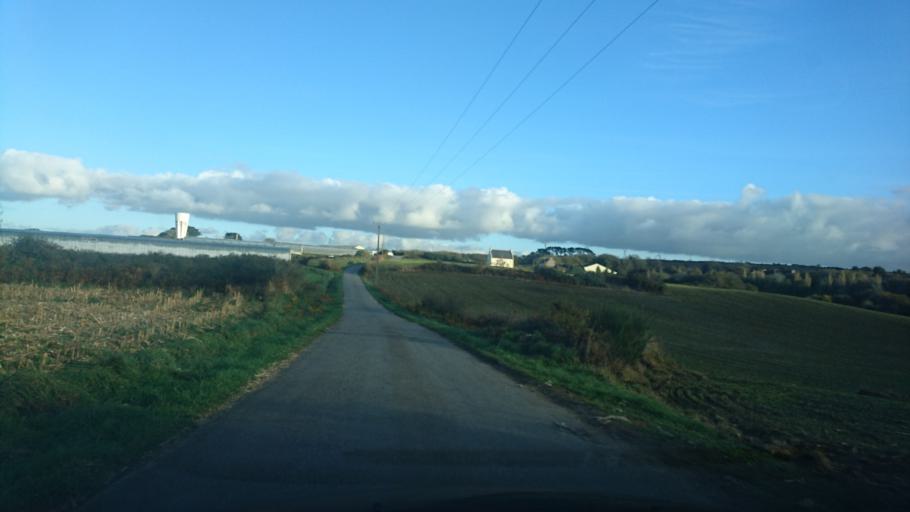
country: FR
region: Brittany
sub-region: Departement du Finistere
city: Lampaul-Plouarzel
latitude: 48.4387
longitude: -4.7658
